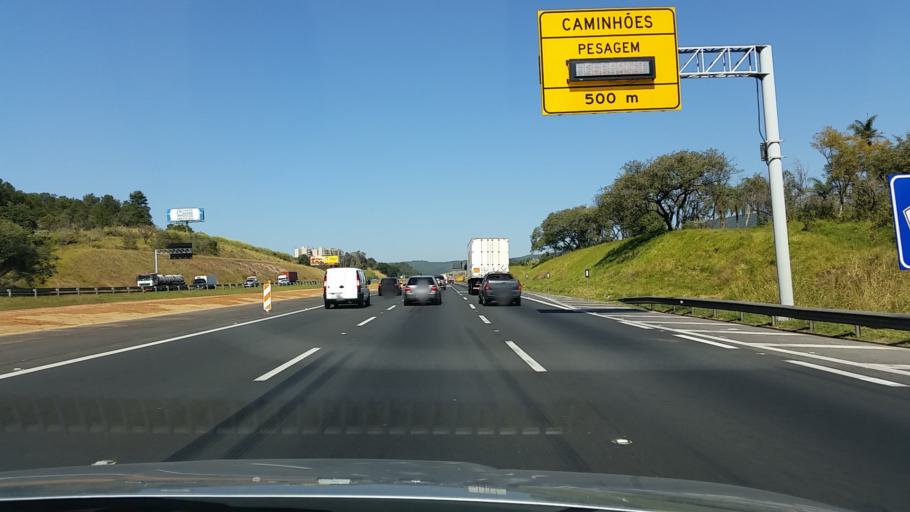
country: BR
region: Sao Paulo
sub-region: Jundiai
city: Jundiai
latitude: -23.1777
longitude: -46.9360
